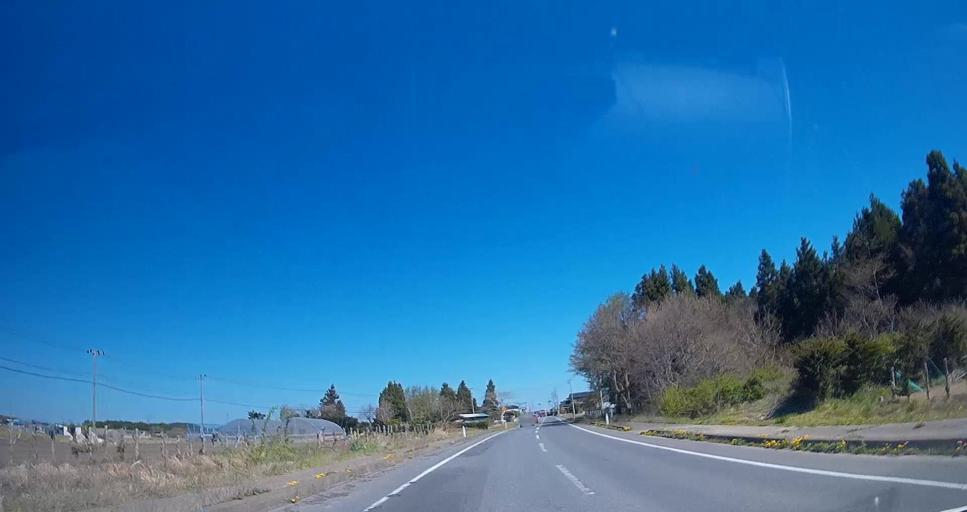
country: JP
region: Aomori
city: Misawa
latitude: 40.6213
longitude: 141.4498
